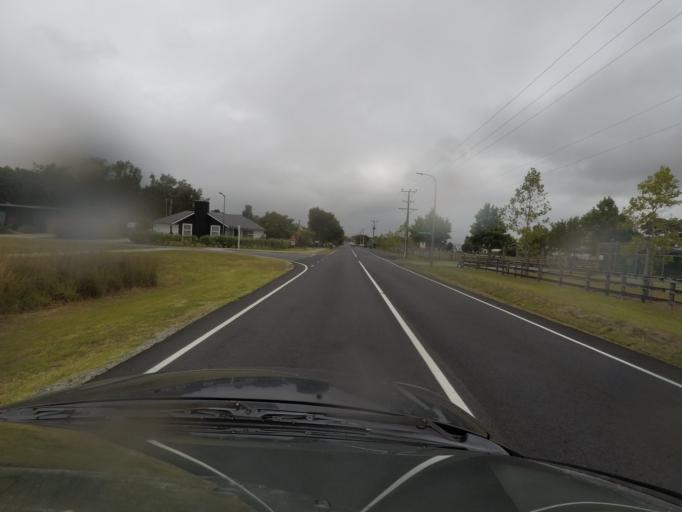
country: NZ
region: Auckland
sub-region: Auckland
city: Warkworth
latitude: -36.3480
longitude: 174.7123
